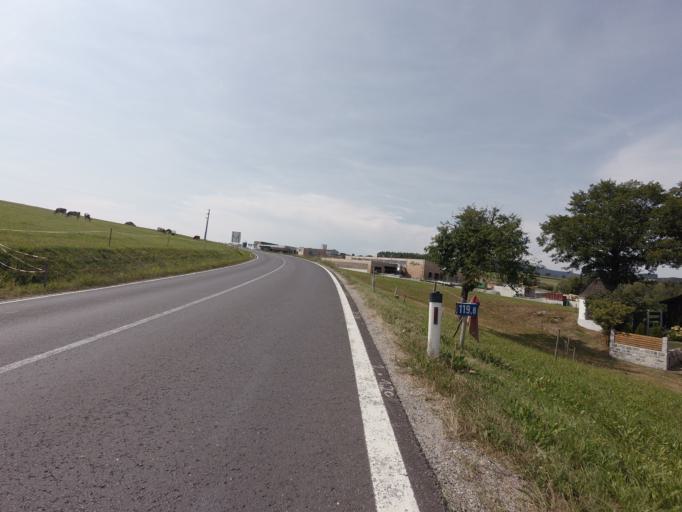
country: AT
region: Upper Austria
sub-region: Politischer Bezirk Urfahr-Umgebung
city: Bad Leonfelden
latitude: 48.5236
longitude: 14.3126
